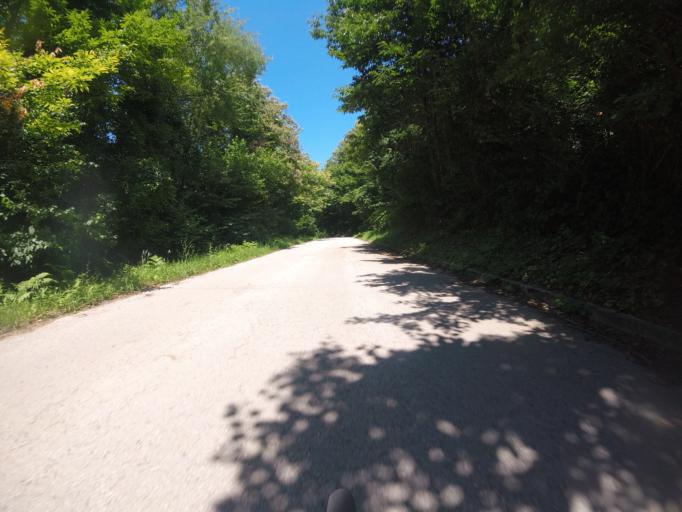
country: HR
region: Karlovacka
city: Ozalj
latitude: 45.6755
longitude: 15.4389
